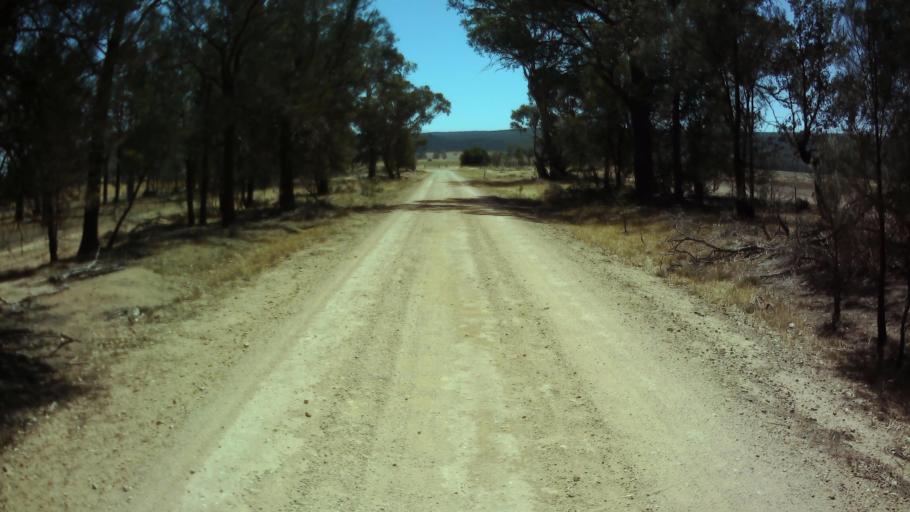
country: AU
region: New South Wales
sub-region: Weddin
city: Grenfell
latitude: -33.9946
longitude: 147.9580
